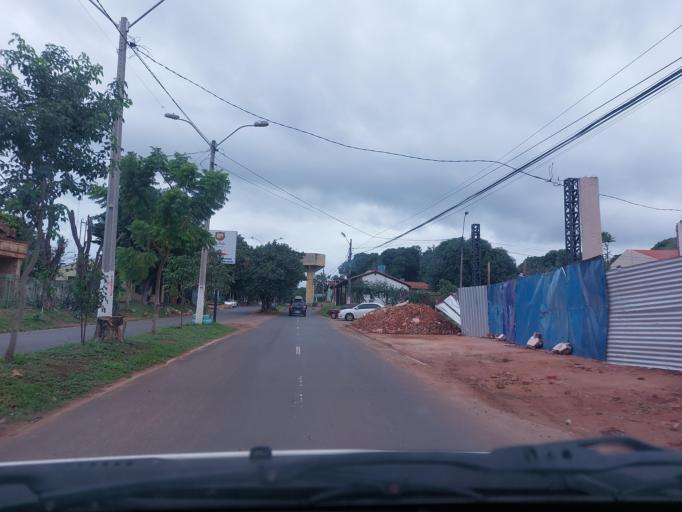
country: PY
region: San Pedro
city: Guayaybi
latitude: -24.6710
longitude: -56.4424
